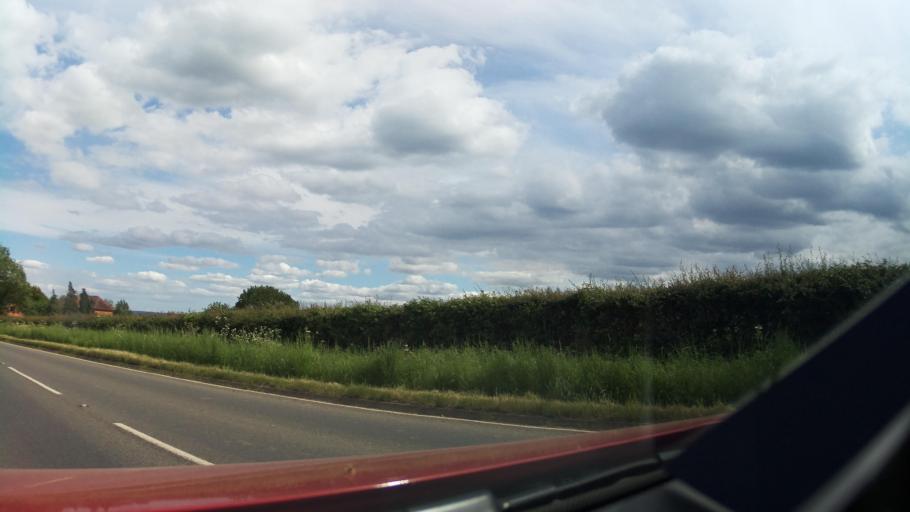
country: GB
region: England
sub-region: Worcestershire
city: Pershore
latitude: 52.1026
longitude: -2.0403
